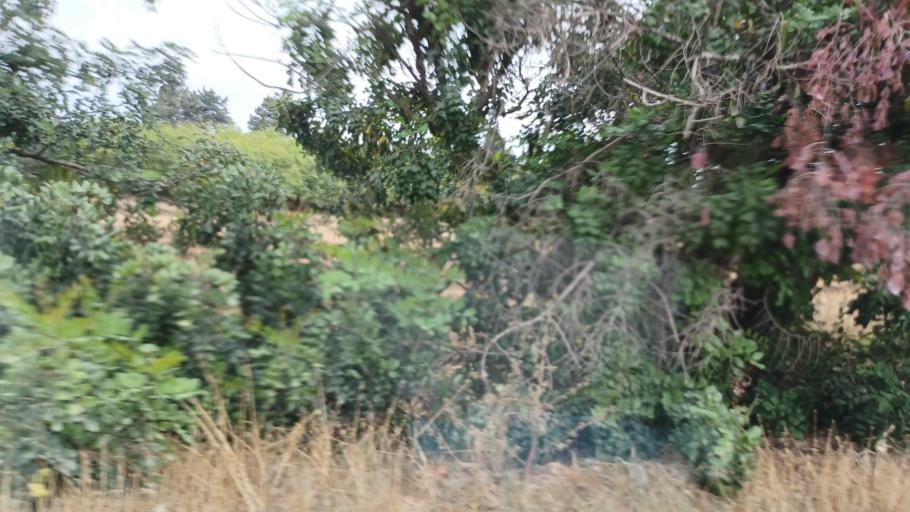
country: CY
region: Ammochostos
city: Ayia Napa
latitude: 35.0129
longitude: 34.0211
